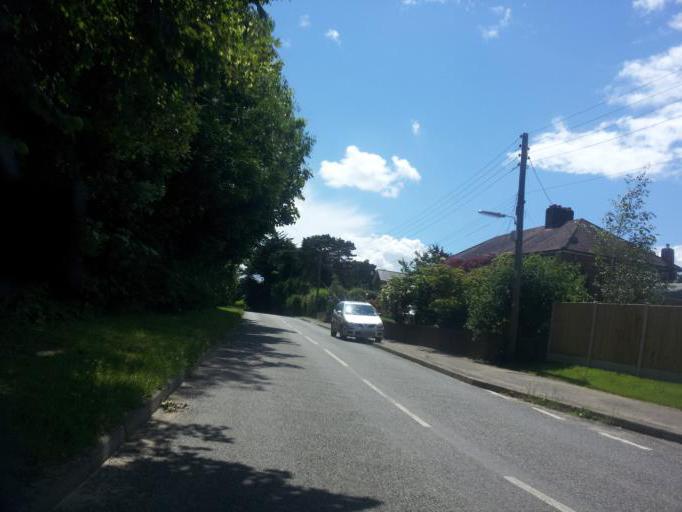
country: GB
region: England
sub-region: Kent
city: West Malling
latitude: 51.3112
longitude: 0.3875
